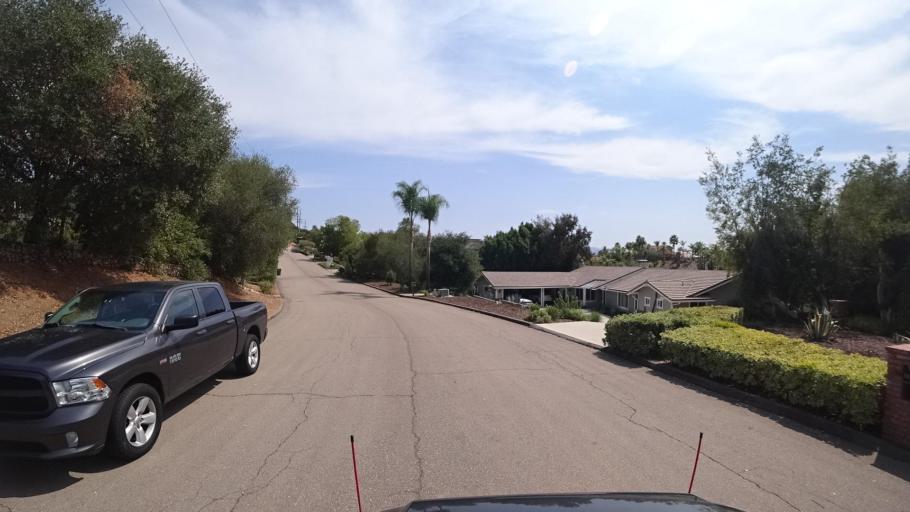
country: US
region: California
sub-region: San Diego County
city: Escondido
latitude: 33.0929
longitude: -117.0463
